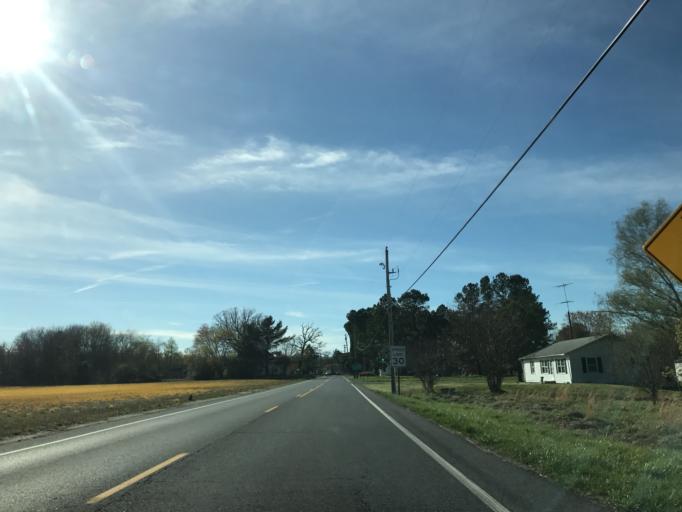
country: US
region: Maryland
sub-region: Caroline County
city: Greensboro
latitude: 39.0367
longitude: -75.7819
